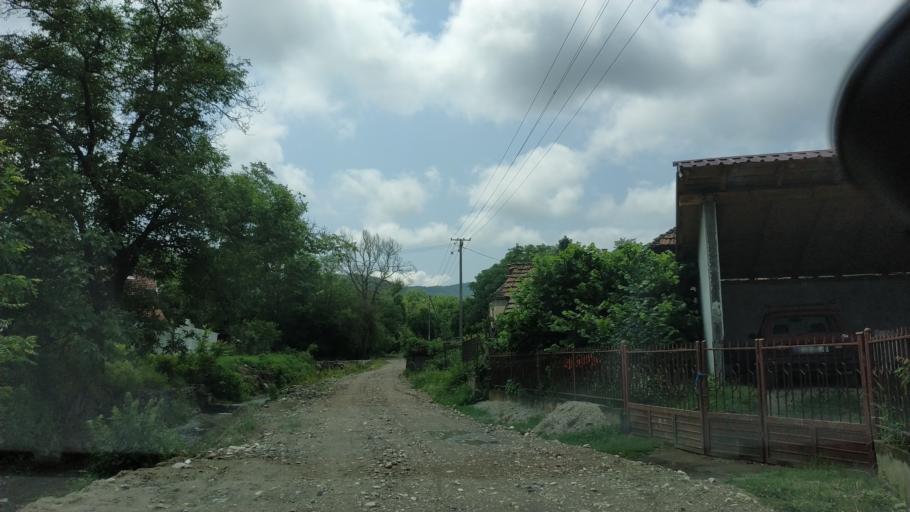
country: RS
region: Central Serbia
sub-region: Nisavski Okrug
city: Aleksinac
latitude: 43.4204
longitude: 21.7013
